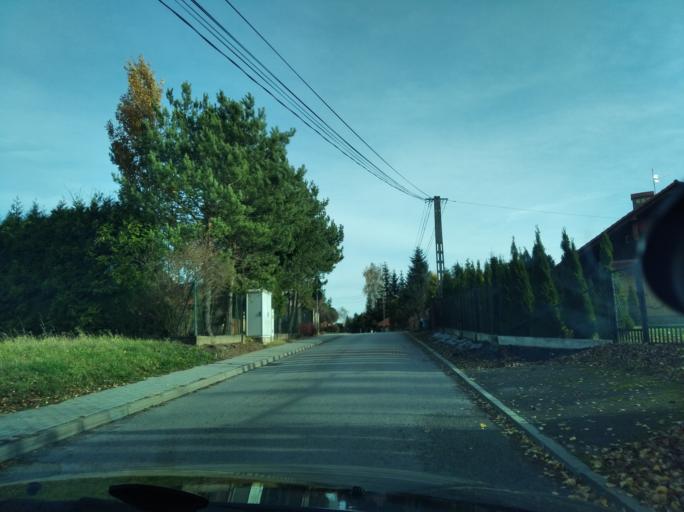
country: PL
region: Subcarpathian Voivodeship
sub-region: Powiat rzeszowski
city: Krasne
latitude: 50.0074
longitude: 22.0901
